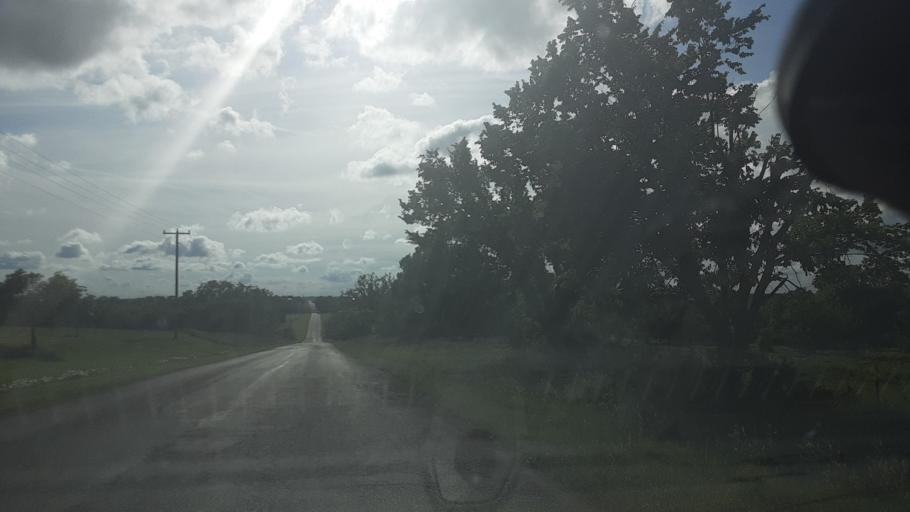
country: US
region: Oklahoma
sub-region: Logan County
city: Langston
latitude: 36.0577
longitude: -97.3651
